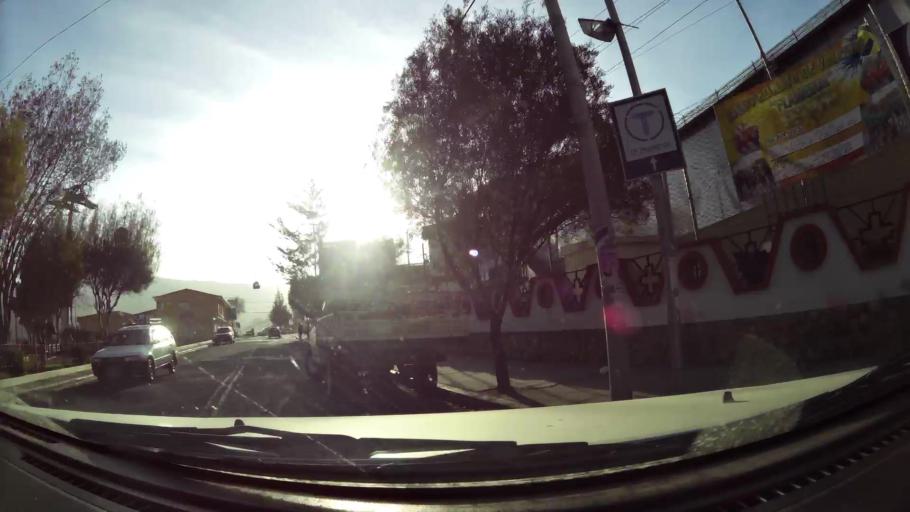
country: BO
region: La Paz
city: La Paz
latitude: -16.5238
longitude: -68.1053
